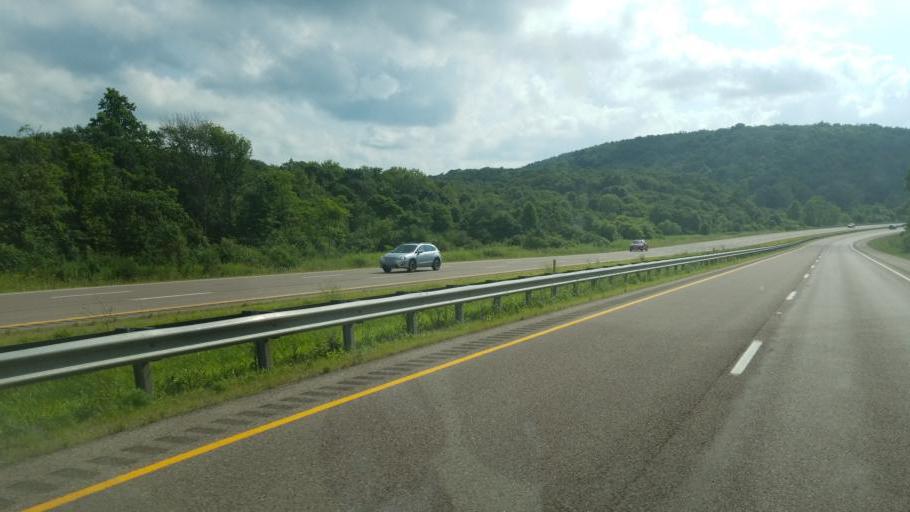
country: US
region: Maryland
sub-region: Garrett County
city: Oakland
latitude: 39.6985
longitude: -79.3177
